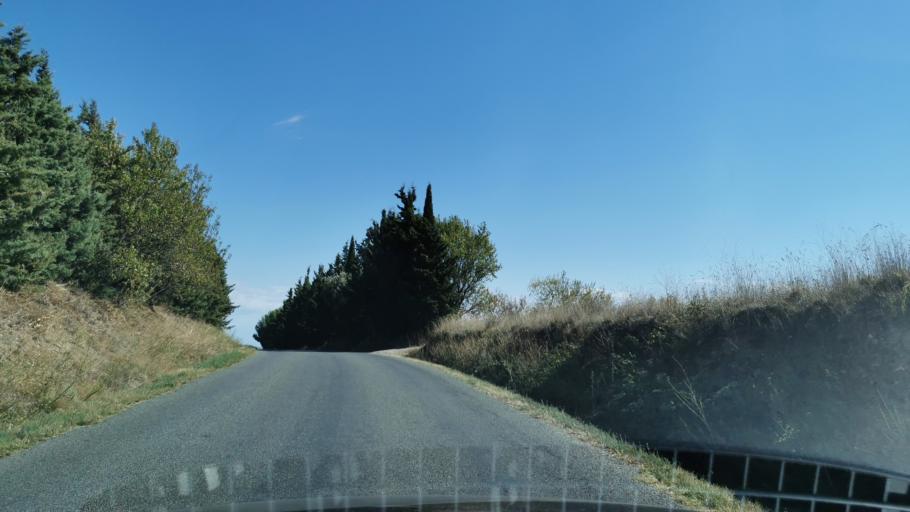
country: FR
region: Languedoc-Roussillon
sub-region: Departement de l'Aude
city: Caunes-Minervois
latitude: 43.3216
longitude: 2.5381
